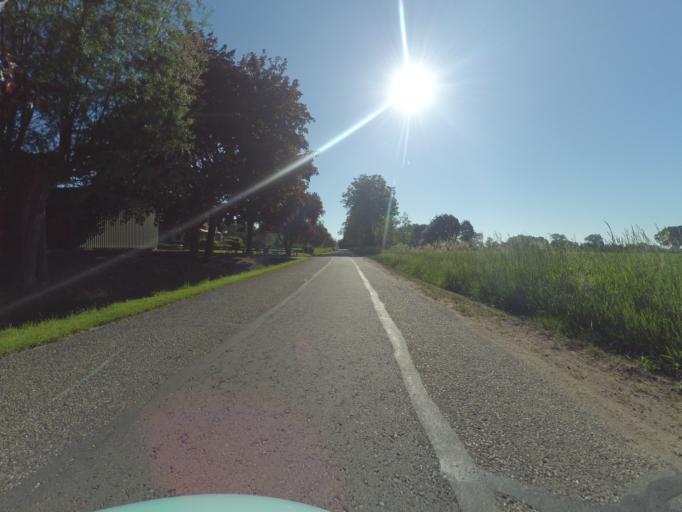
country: NL
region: Gelderland
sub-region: Gemeente Voorst
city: Voorst
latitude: 52.1713
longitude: 6.1199
